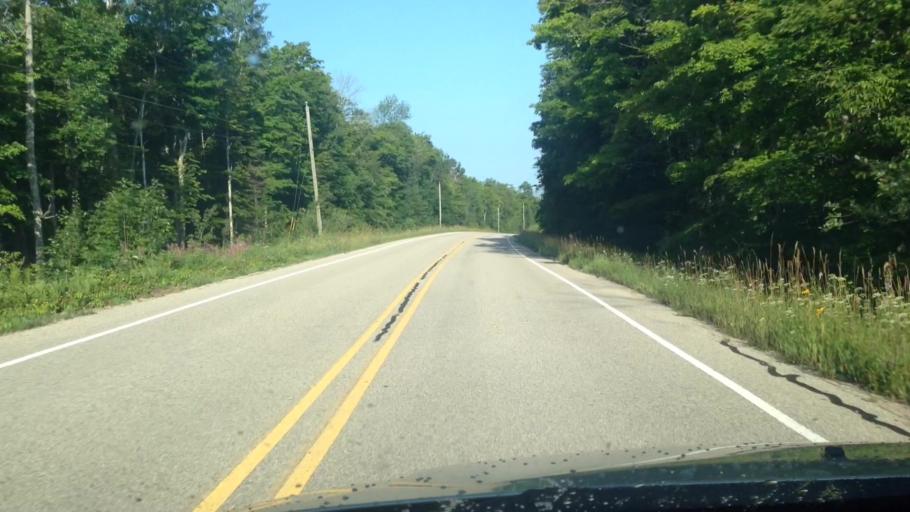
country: US
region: Michigan
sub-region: Mackinac County
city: Saint Ignace
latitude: 45.8931
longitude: -84.8035
